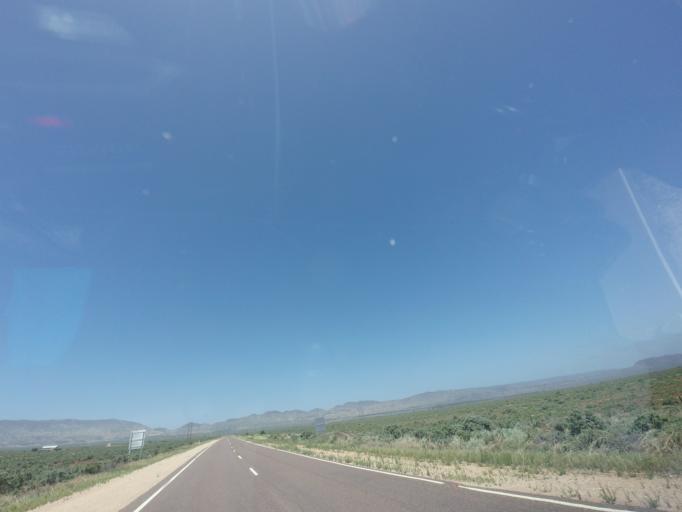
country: AU
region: South Australia
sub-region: Port Augusta
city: Port Augusta
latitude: -32.6261
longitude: 137.9270
